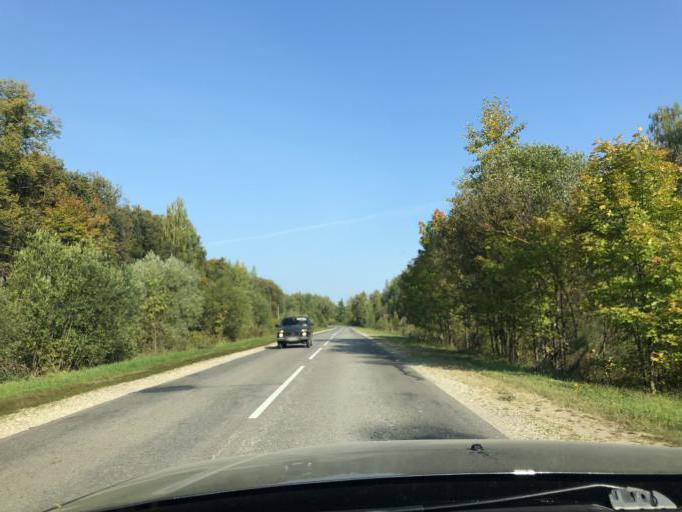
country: RU
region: Tula
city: Leninskiy
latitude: 54.3284
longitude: 37.3937
